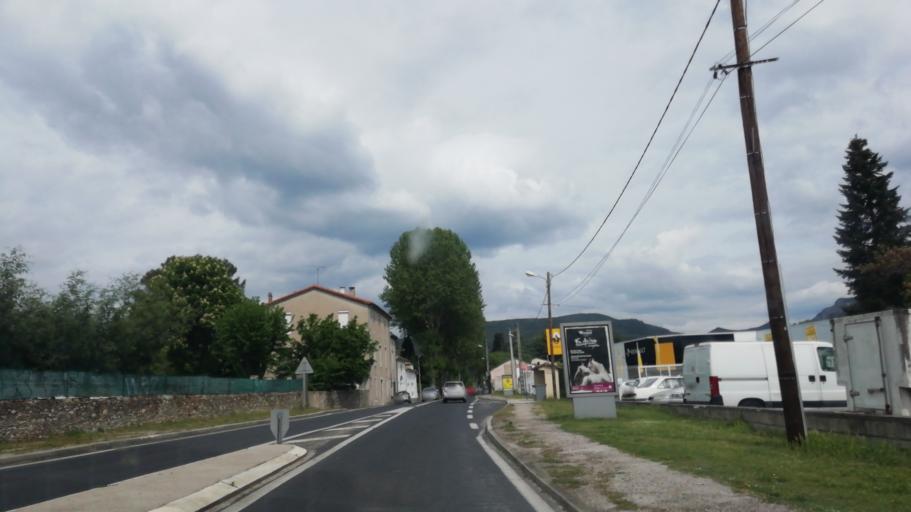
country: FR
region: Languedoc-Roussillon
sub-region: Departement de l'Herault
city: Laroque
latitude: 43.9267
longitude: 3.7155
